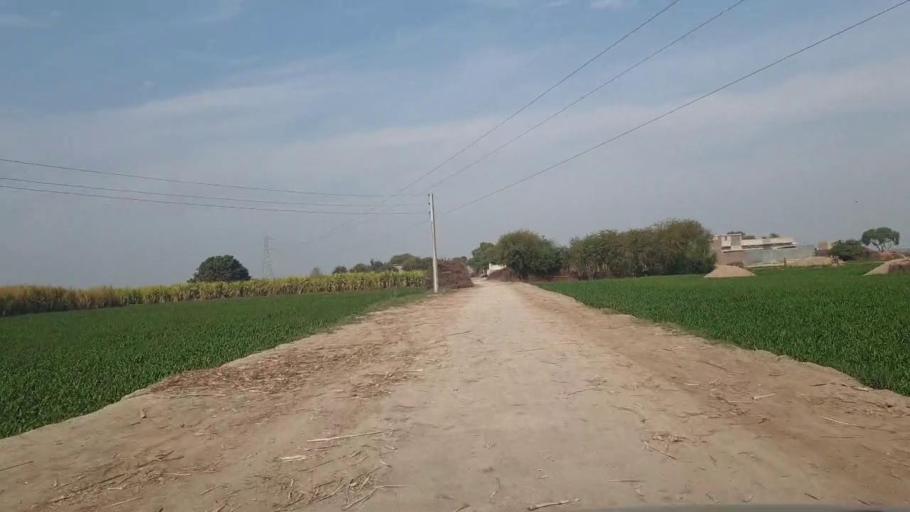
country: PK
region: Sindh
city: Shahdadpur
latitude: 25.8846
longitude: 68.6125
